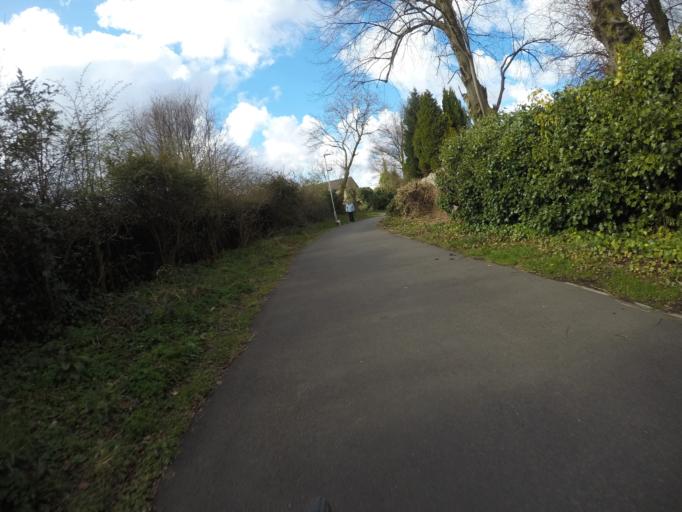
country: GB
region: Scotland
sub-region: North Ayrshire
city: Beith
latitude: 55.7452
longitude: -4.6416
